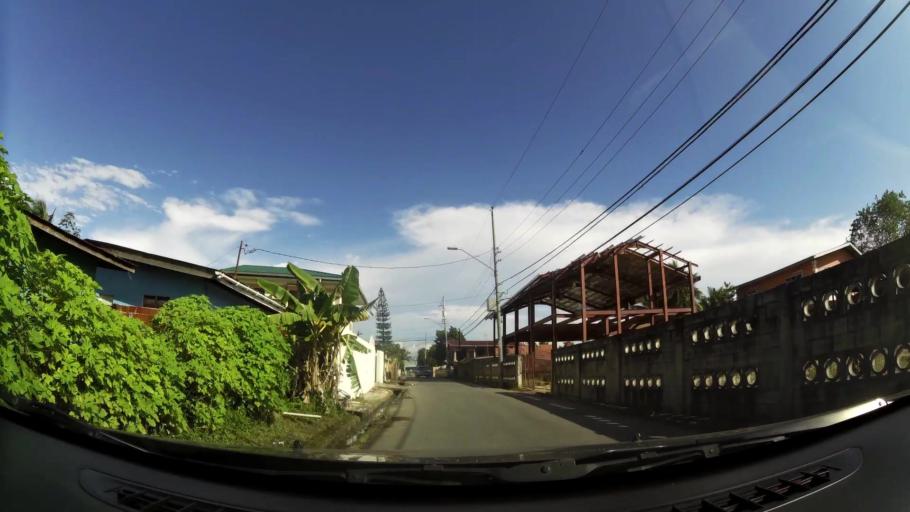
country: TT
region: Chaguanas
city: Chaguanas
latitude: 10.5269
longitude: -61.3913
